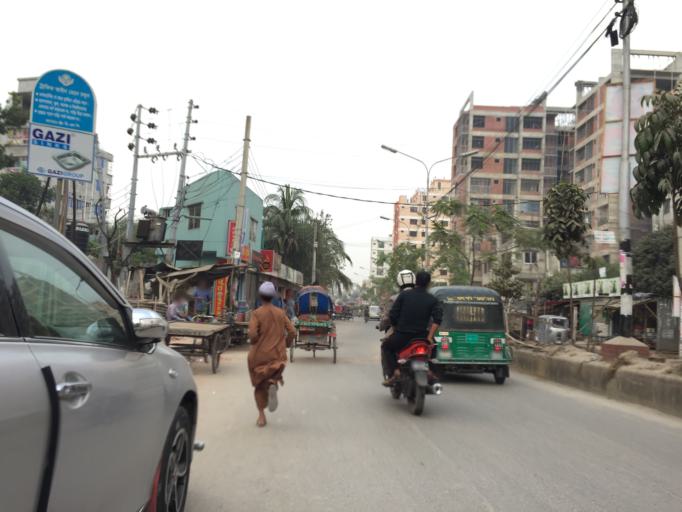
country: BD
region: Dhaka
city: Azimpur
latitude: 23.7970
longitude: 90.3650
